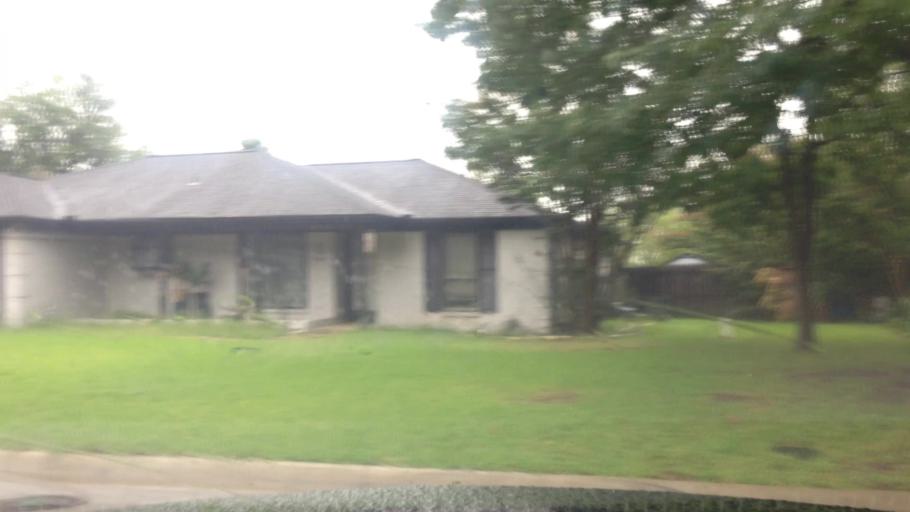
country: US
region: Texas
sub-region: Tarrant County
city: Watauga
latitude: 32.8805
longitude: -97.2311
